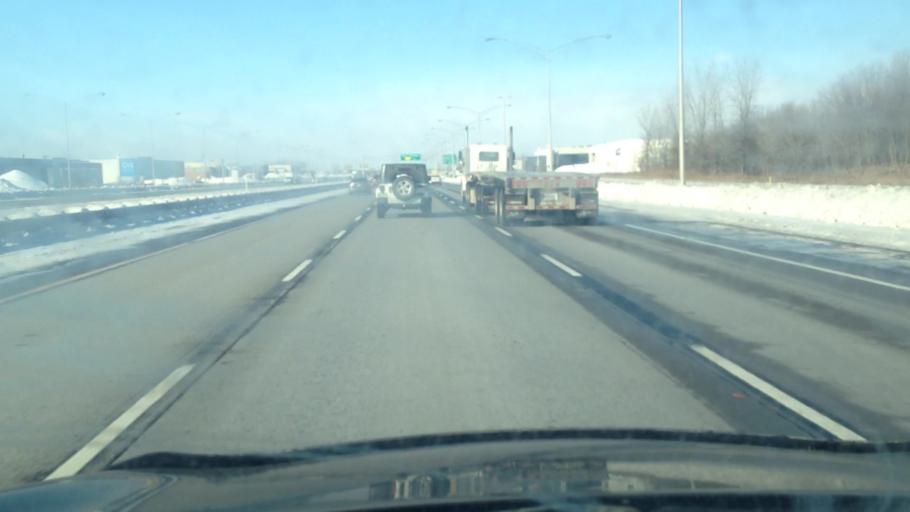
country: CA
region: Quebec
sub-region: Laurentides
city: Boisbriand
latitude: 45.5581
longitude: -73.8127
